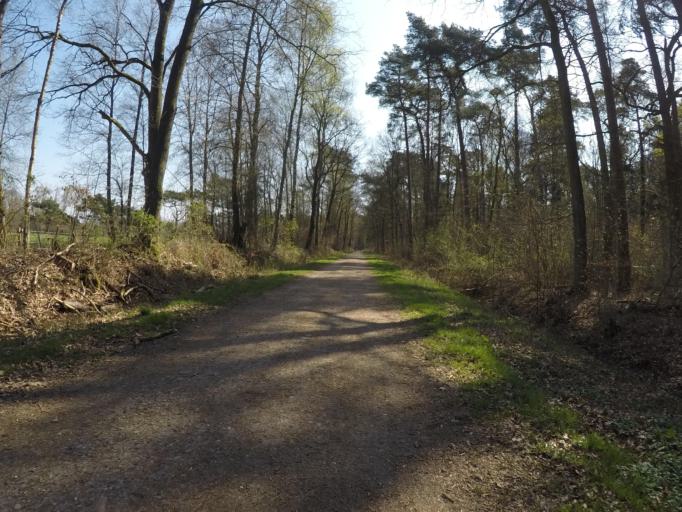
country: DE
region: Schleswig-Holstein
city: Rellingen
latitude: 53.6146
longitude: 9.7761
